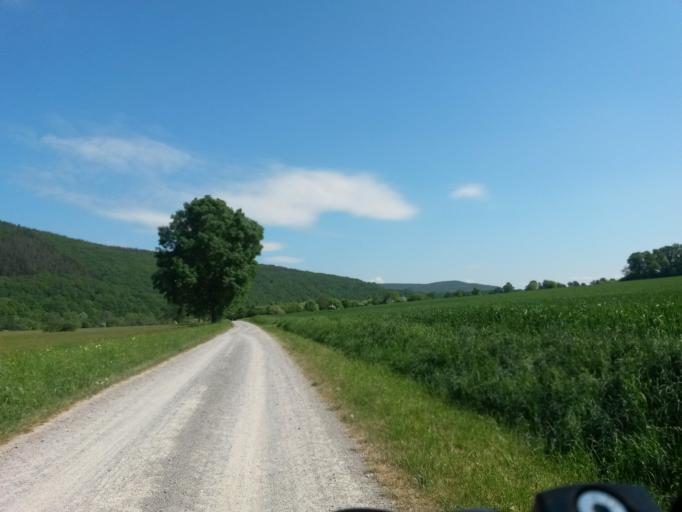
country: DE
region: Bavaria
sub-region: Regierungsbezirk Unterfranken
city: Bad Bocklet
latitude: 50.2728
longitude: 10.0618
